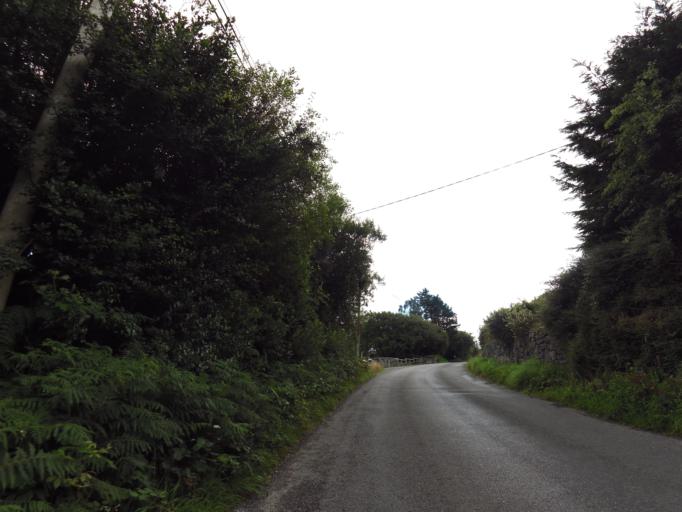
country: IE
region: Connaught
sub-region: County Galway
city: Oughterard
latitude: 53.4186
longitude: -9.3289
